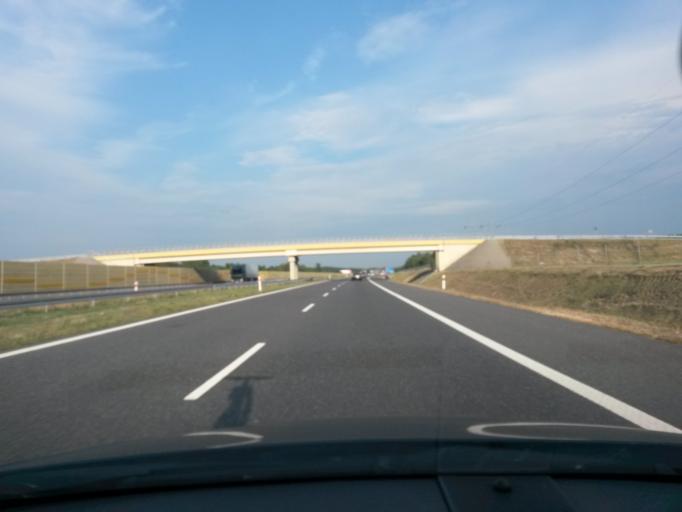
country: PL
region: Lodz Voivodeship
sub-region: Powiat zgierski
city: Ozorkow
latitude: 51.9272
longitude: 19.3197
